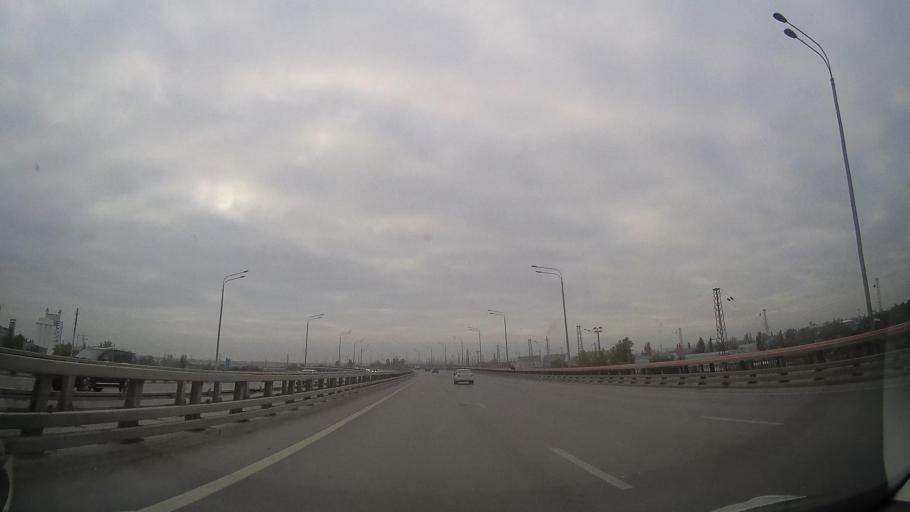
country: RU
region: Rostov
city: Rostov-na-Donu
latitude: 47.2081
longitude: 39.7043
